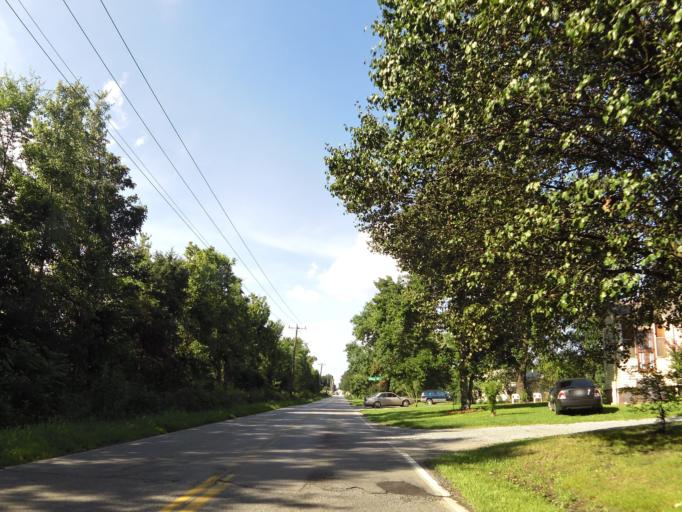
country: US
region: Tennessee
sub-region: Blount County
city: Alcoa
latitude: 35.8110
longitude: -83.9618
